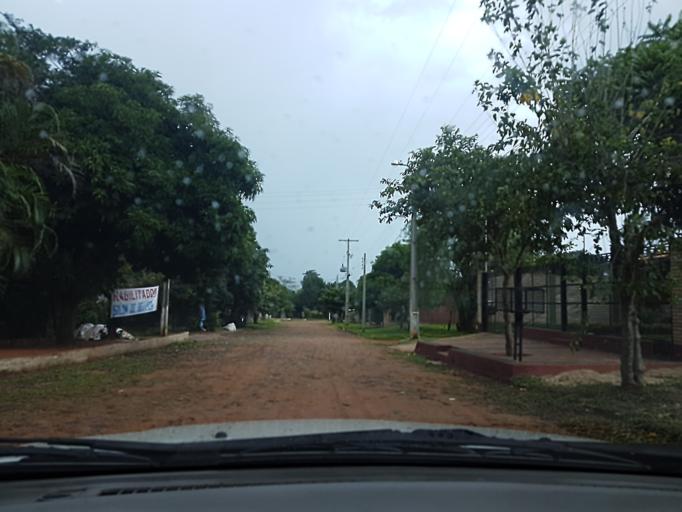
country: PY
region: Central
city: Capiata
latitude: -25.2776
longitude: -57.4593
